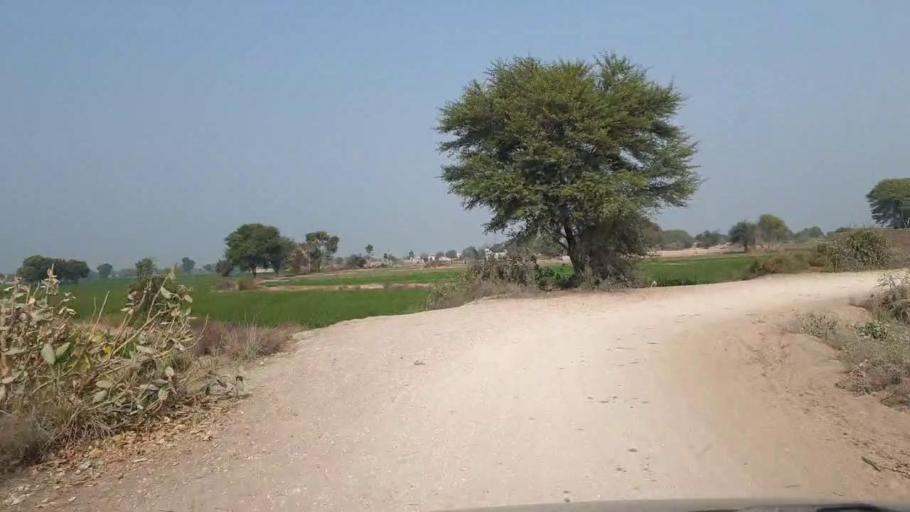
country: PK
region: Sindh
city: Bhit Shah
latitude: 25.8352
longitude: 68.5004
